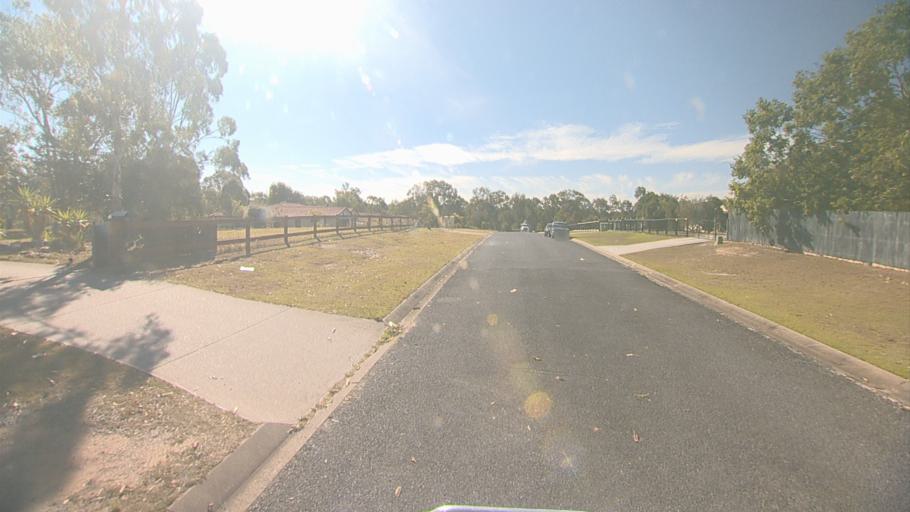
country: AU
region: Queensland
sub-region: Ipswich
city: Springfield Lakes
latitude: -27.7296
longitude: 152.9420
